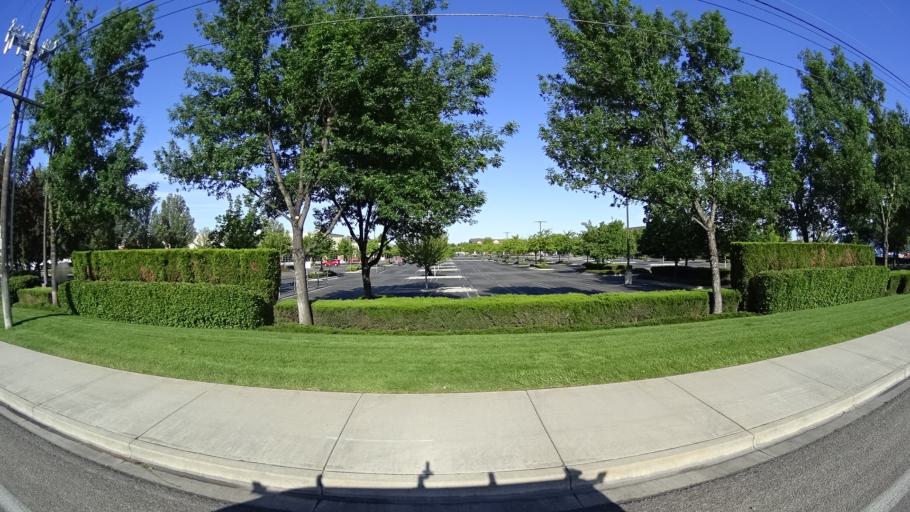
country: US
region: Idaho
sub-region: Ada County
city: Garden City
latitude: 43.5860
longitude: -116.2743
